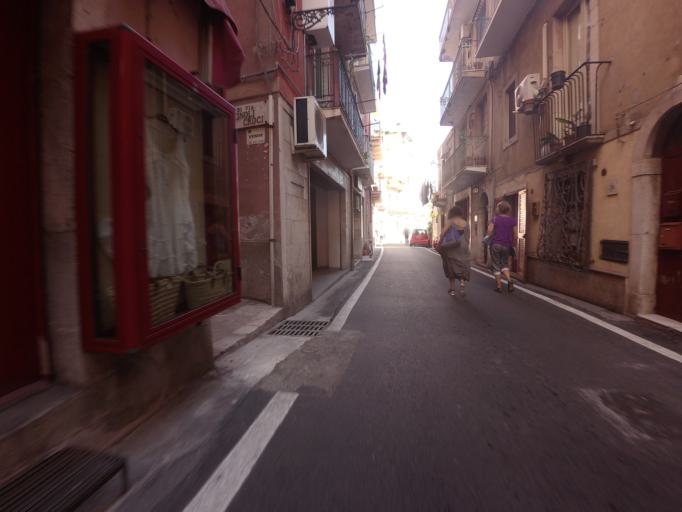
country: IT
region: Sicily
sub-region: Messina
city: Taormina
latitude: 37.8518
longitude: 15.2888
